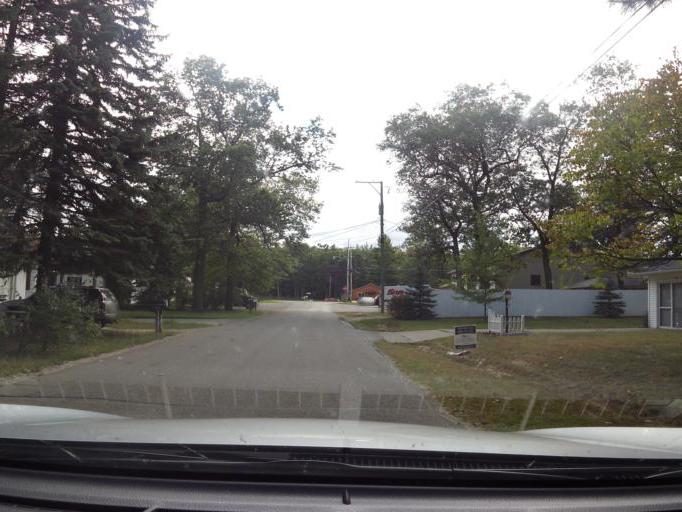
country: US
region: Michigan
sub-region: Roscommon County
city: Prudenville
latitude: 44.2996
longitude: -84.7029
